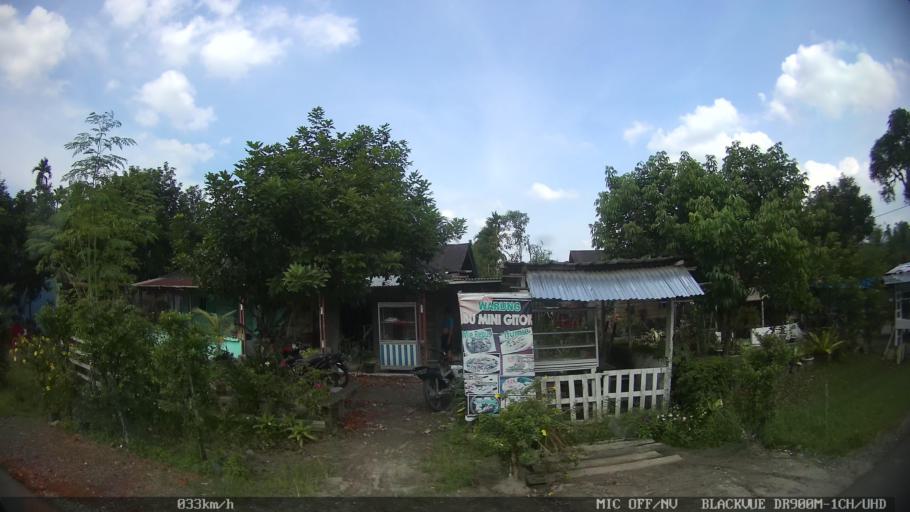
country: ID
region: North Sumatra
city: Binjai
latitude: 3.6422
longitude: 98.5176
